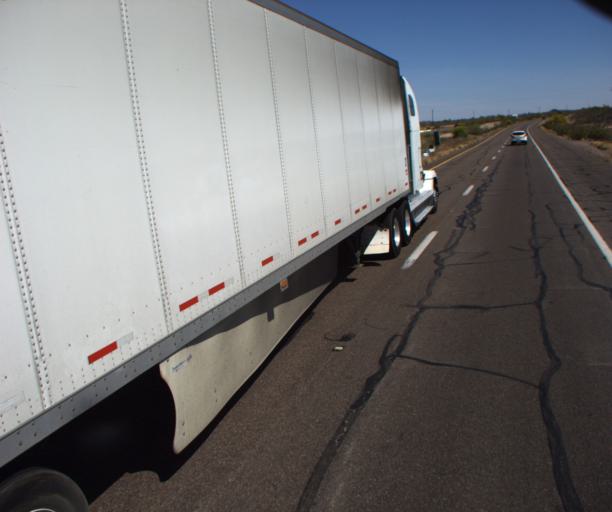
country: US
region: Arizona
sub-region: Maricopa County
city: Gila Bend
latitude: 32.8543
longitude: -113.2518
